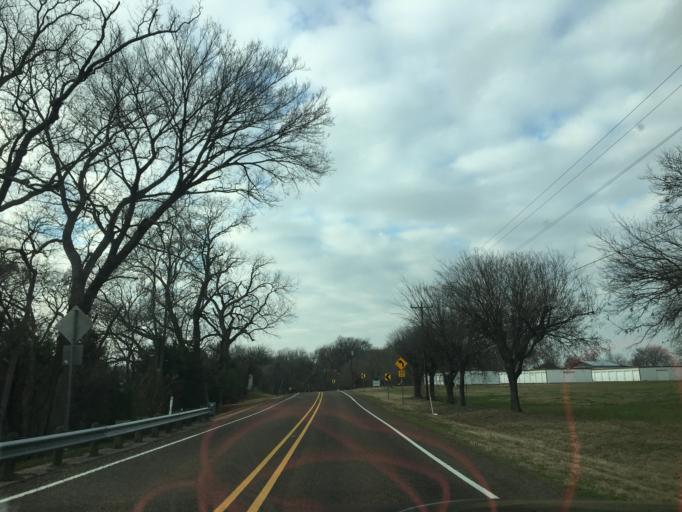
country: US
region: Texas
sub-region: Ellis County
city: Palmer
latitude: 32.4488
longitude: -96.7239
